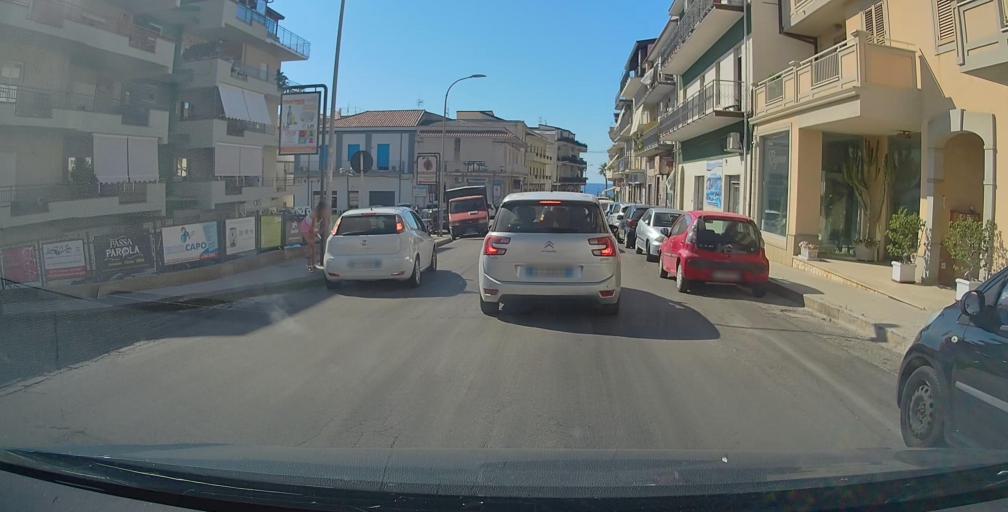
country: IT
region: Sicily
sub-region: Messina
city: Capo d'Orlando
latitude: 38.1630
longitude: 14.7480
